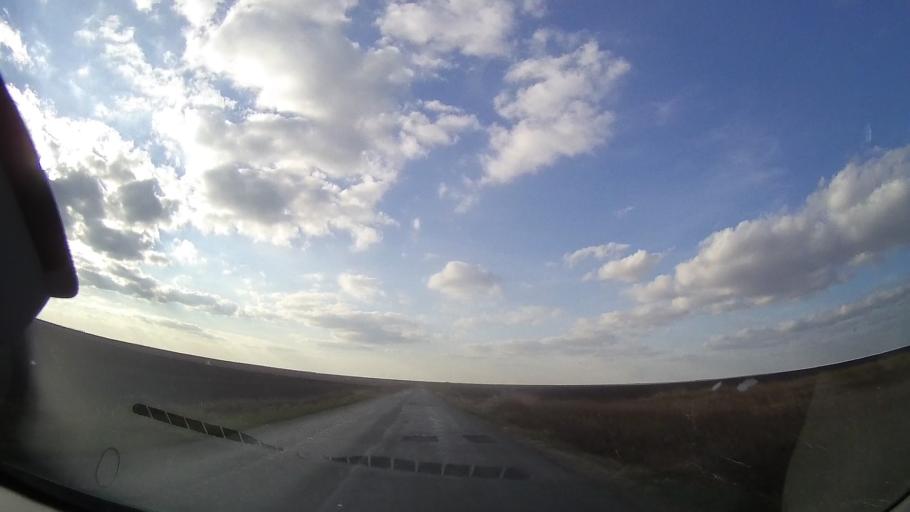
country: RO
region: Constanta
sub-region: Comuna Negru Voda
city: Negru Voda
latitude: 43.8202
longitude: 28.1740
